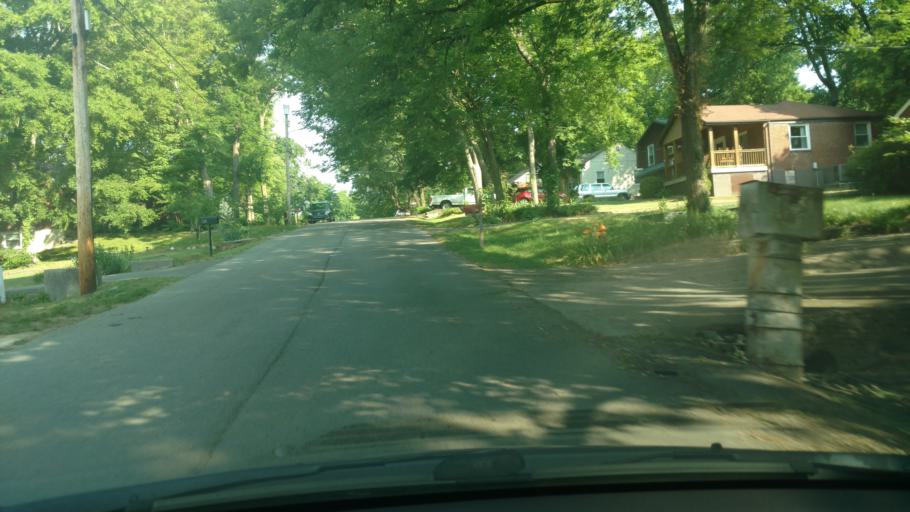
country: US
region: Tennessee
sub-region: Davidson County
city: Lakewood
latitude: 36.2182
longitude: -86.7137
